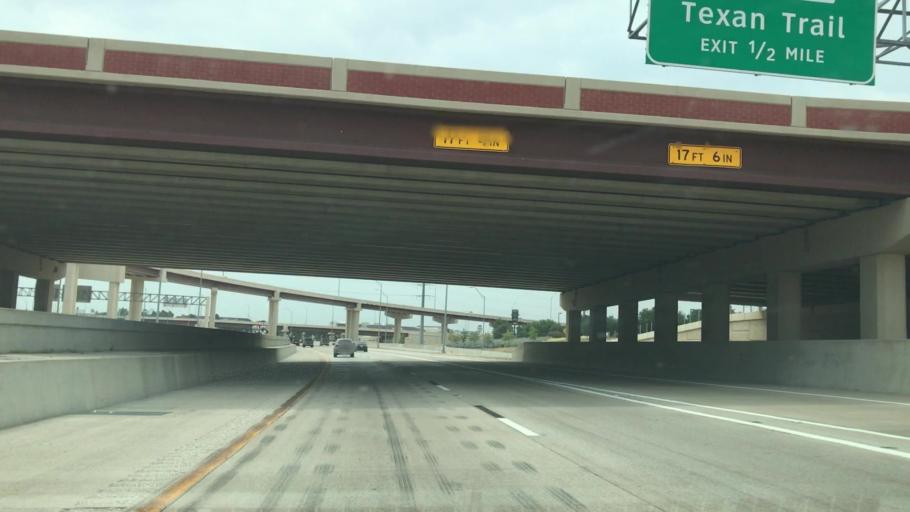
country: US
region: Texas
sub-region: Tarrant County
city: Grapevine
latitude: 32.9252
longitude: -97.0890
